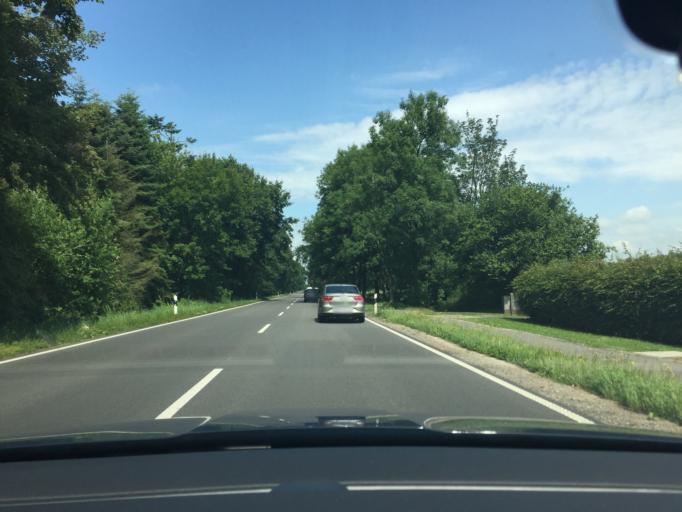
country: DE
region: Lower Saxony
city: Hesel
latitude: 53.3167
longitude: 7.5977
